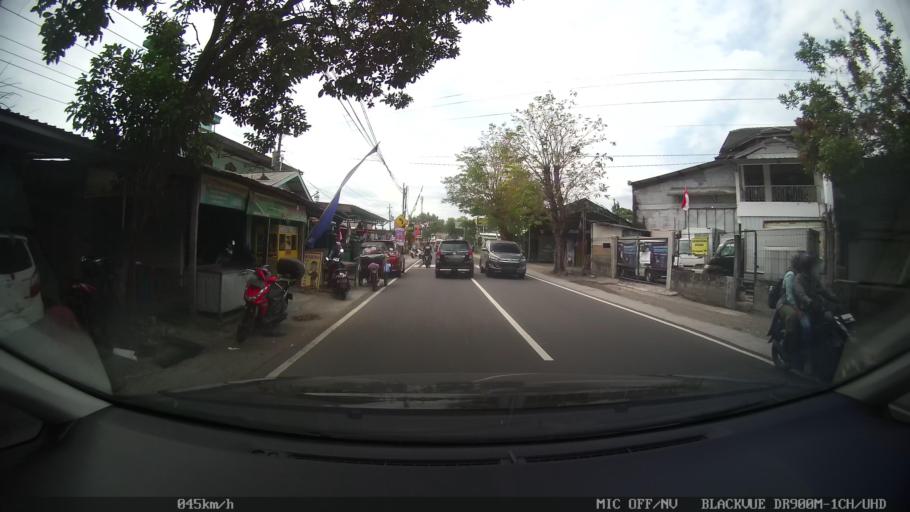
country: ID
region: Central Java
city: Candi Prambanan
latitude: -7.7652
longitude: 110.4883
